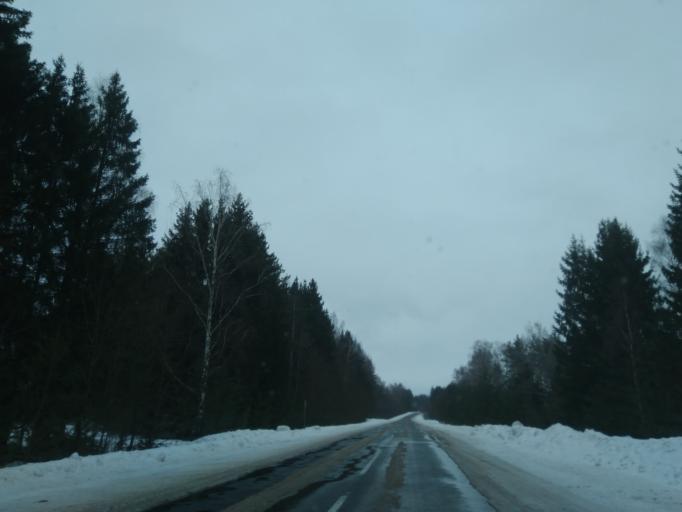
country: BY
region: Minsk
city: Ivyanyets
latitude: 53.8475
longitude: 26.7910
